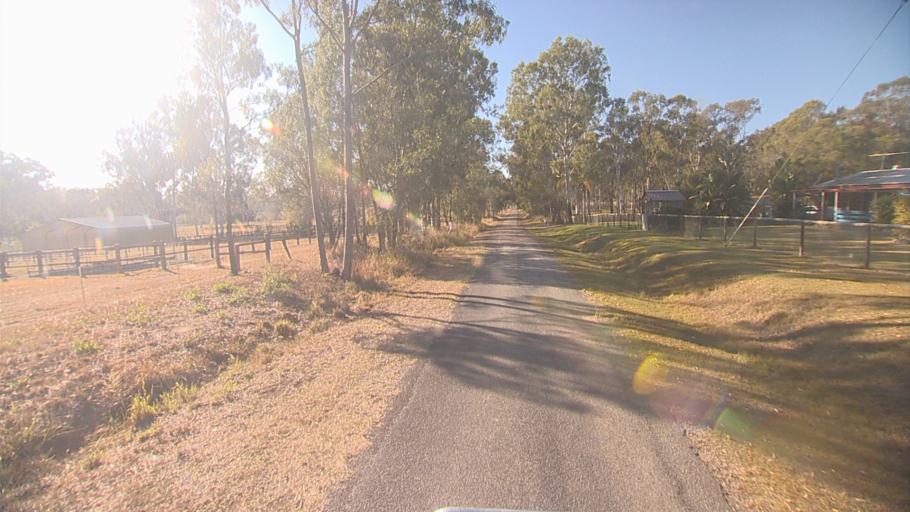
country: AU
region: Queensland
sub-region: Logan
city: North Maclean
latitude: -27.7912
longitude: 152.9901
